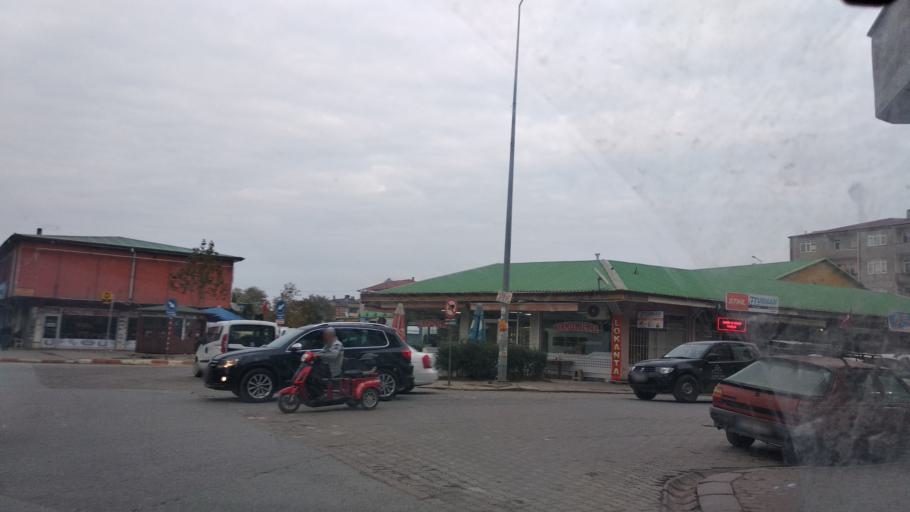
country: TR
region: Sakarya
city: Karasu
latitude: 41.0951
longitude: 30.6870
